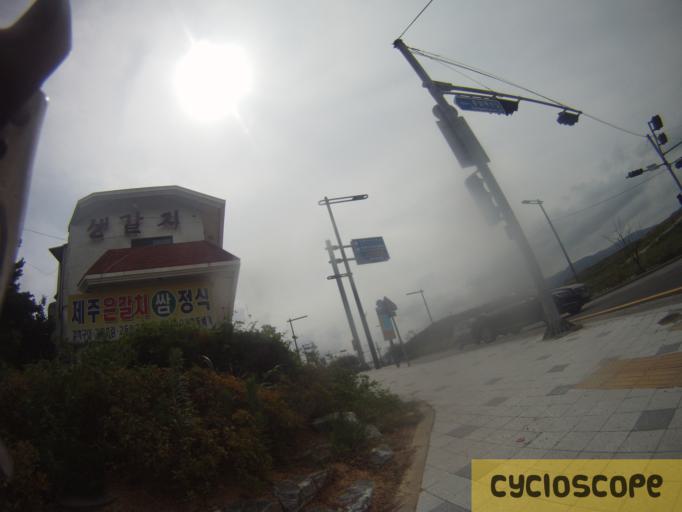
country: KR
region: Busan
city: Kijang
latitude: 35.1929
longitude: 129.2188
